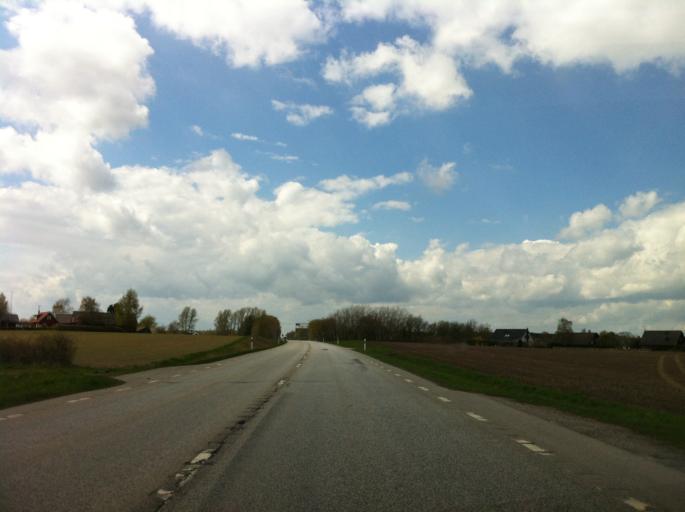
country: SE
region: Skane
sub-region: Eslovs Kommun
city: Stehag
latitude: 55.8504
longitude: 13.4207
